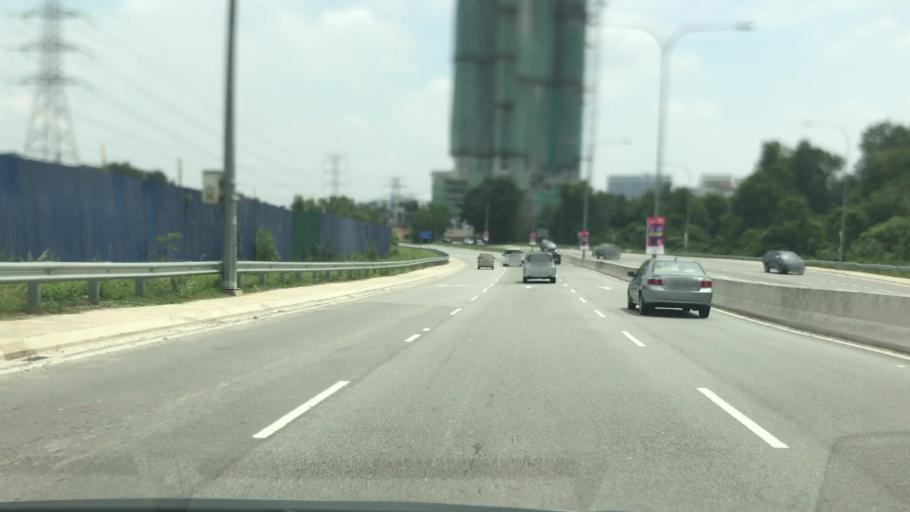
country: MY
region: Selangor
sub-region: Petaling
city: Petaling Jaya
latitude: 3.0537
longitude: 101.6680
